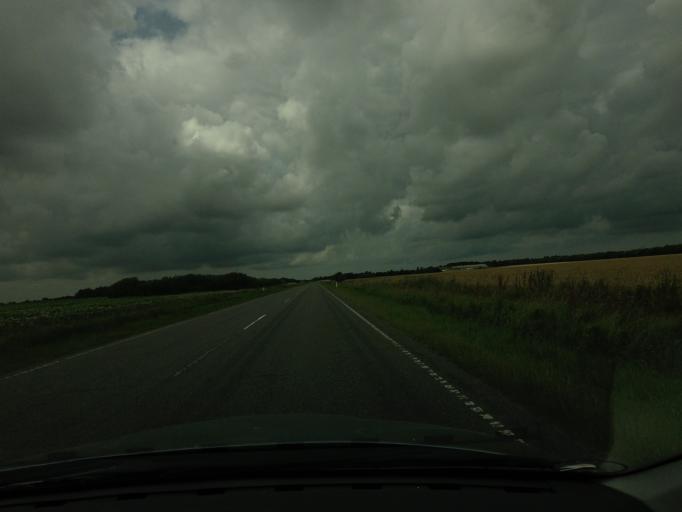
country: DK
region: North Denmark
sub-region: Hjorring Kommune
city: Hjorring
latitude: 57.4234
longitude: 10.0139
